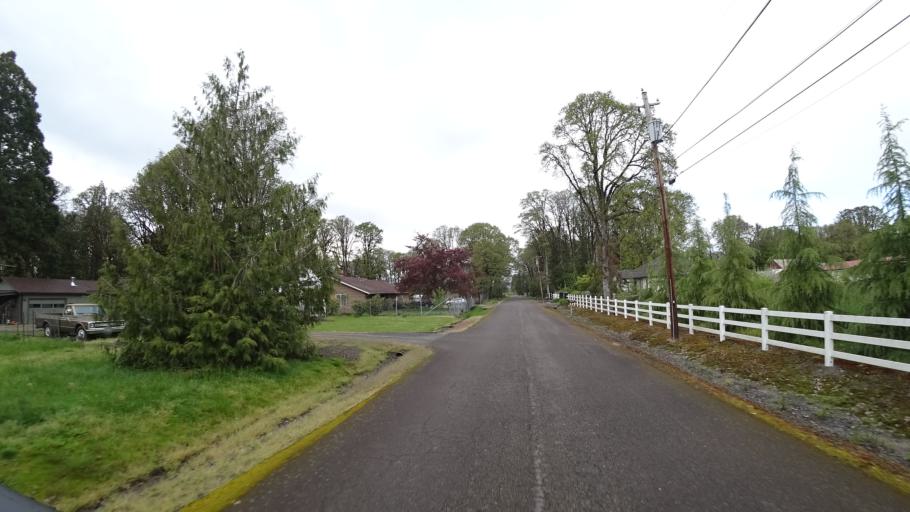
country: US
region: Oregon
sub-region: Washington County
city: Hillsboro
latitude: 45.5552
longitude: -122.9584
